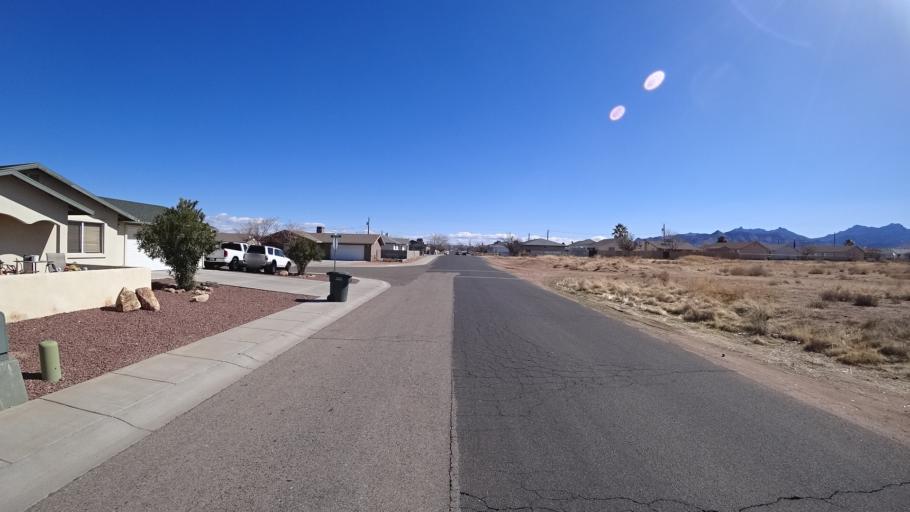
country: US
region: Arizona
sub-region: Mohave County
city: New Kingman-Butler
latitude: 35.2194
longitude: -114.0038
